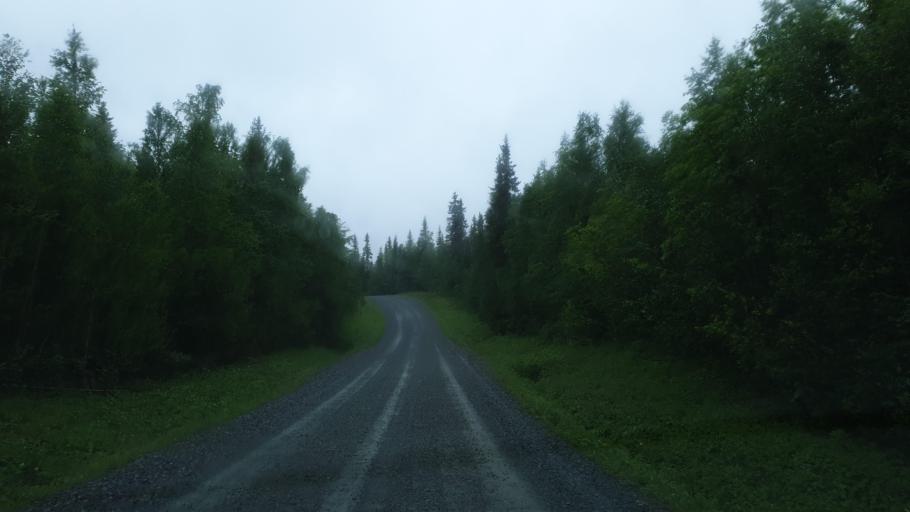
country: SE
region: Vaesterbotten
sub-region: Vilhelmina Kommun
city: Sjoberg
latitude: 65.2734
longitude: 15.9161
